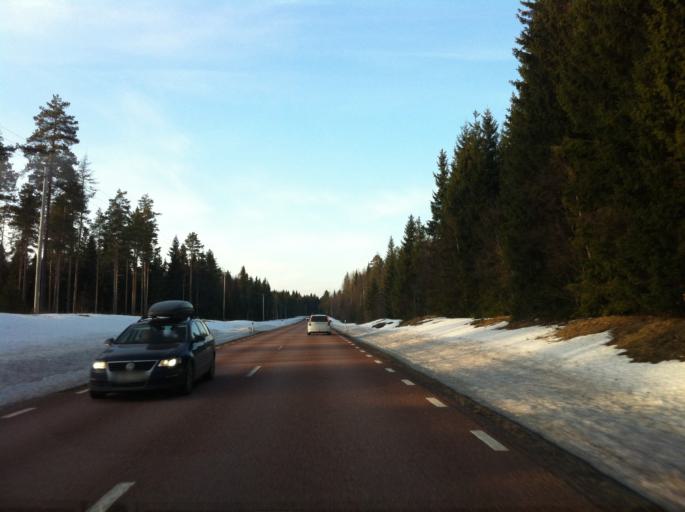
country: SE
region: Dalarna
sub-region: Vansbro Kommun
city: Vansbro
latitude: 60.2651
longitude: 14.1724
